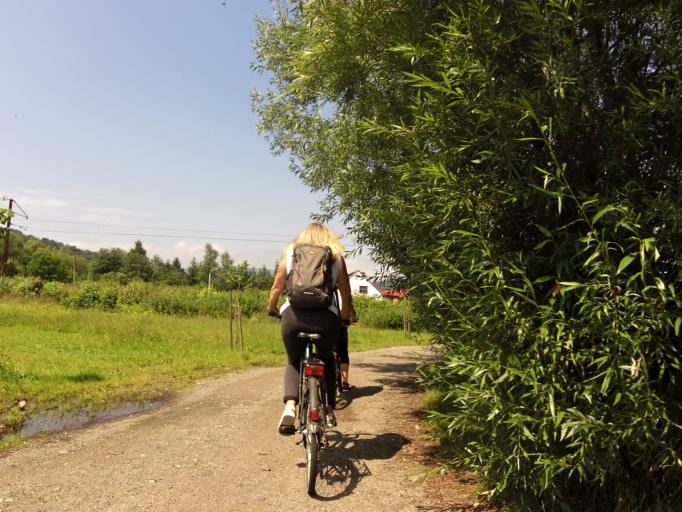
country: PL
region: Silesian Voivodeship
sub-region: Powiat zywiecki
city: Milowka
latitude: 49.5519
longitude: 19.0904
